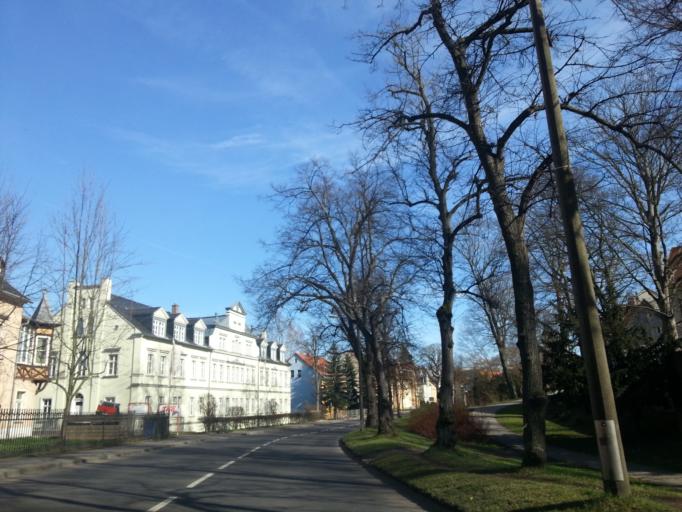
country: DE
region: Saxony
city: Freiberg
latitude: 50.9225
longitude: 13.3453
